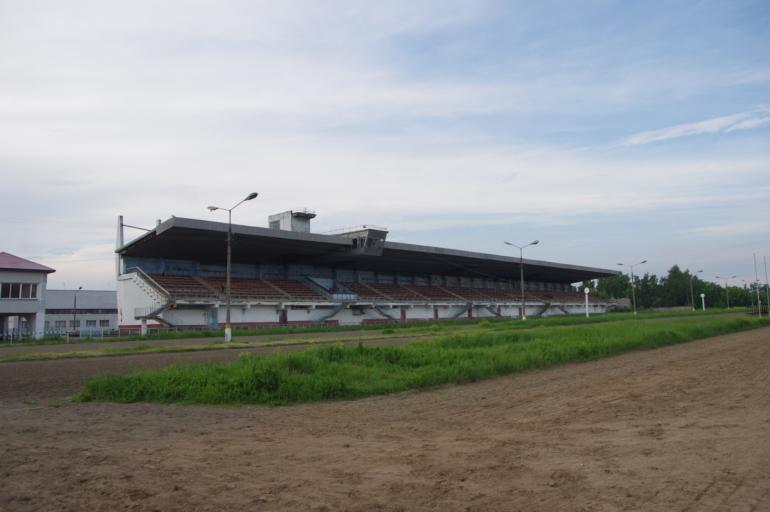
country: RU
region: Moskovskaya
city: Ramenskoye
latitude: 55.5542
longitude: 38.2396
